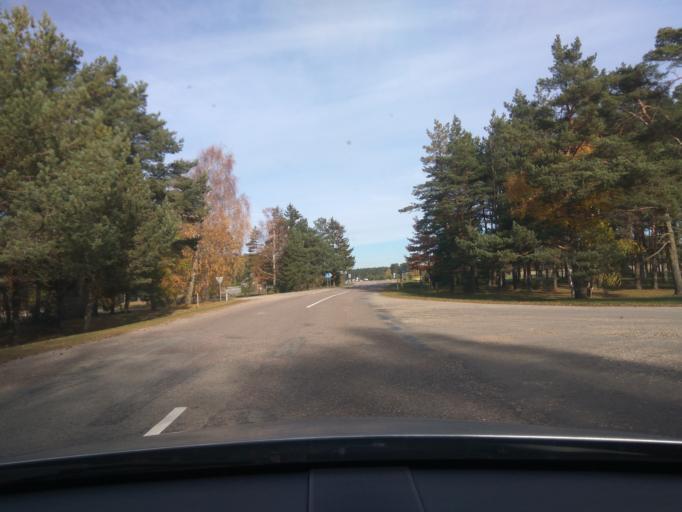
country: LV
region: Alsunga
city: Alsunga
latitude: 57.0061
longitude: 21.3868
